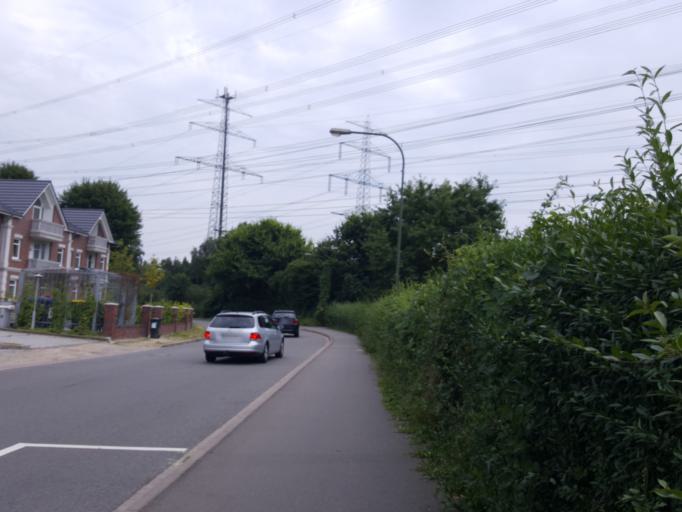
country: DE
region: Schleswig-Holstein
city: Oststeinbek
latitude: 53.5211
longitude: 10.1654
